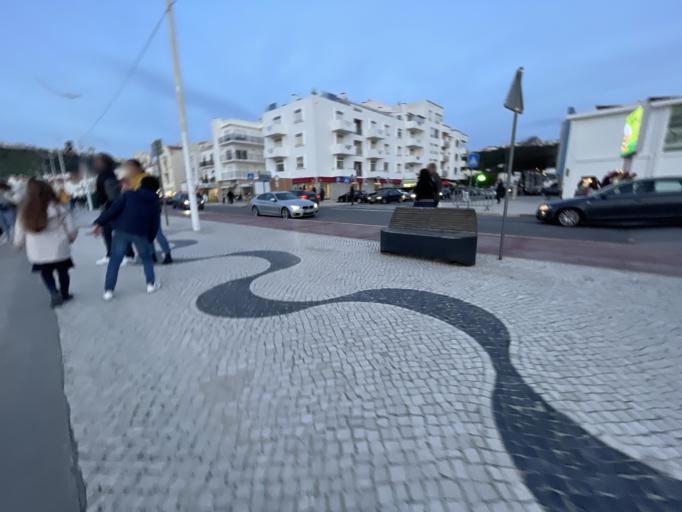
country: PT
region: Leiria
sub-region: Nazare
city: Nazare
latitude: 39.5967
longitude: -9.0724
